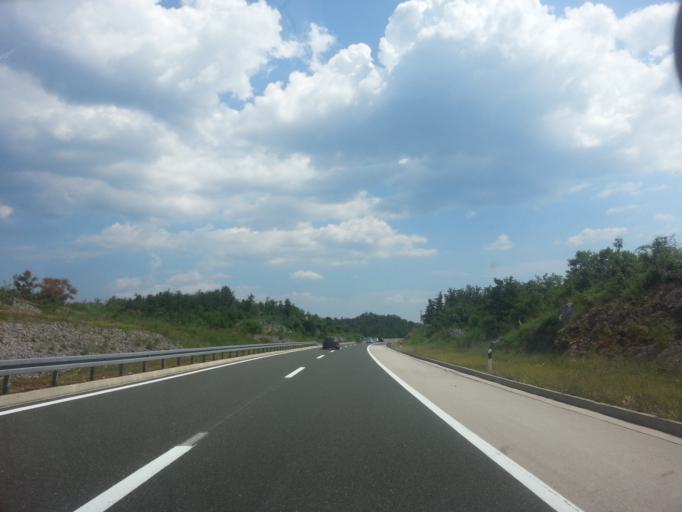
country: HR
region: Primorsko-Goranska
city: Matulji
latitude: 45.4251
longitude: 14.2971
